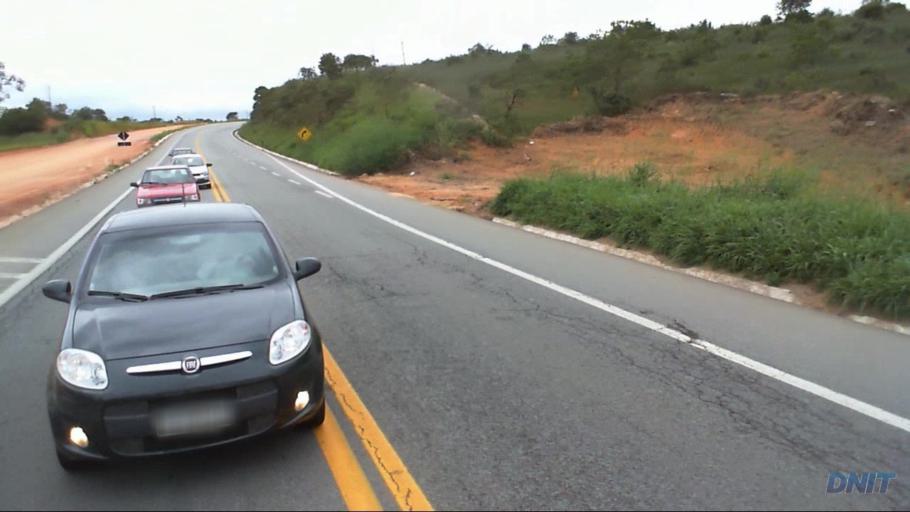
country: BR
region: Minas Gerais
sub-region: Barao De Cocais
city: Barao de Cocais
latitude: -19.7595
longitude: -43.4648
